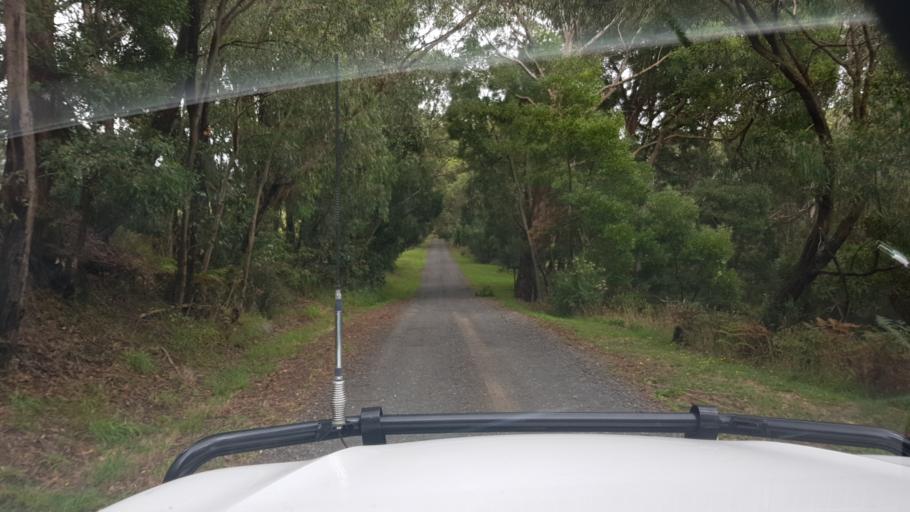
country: AU
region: Victoria
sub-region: Baw Baw
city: Warragul
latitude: -38.0811
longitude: 145.9968
